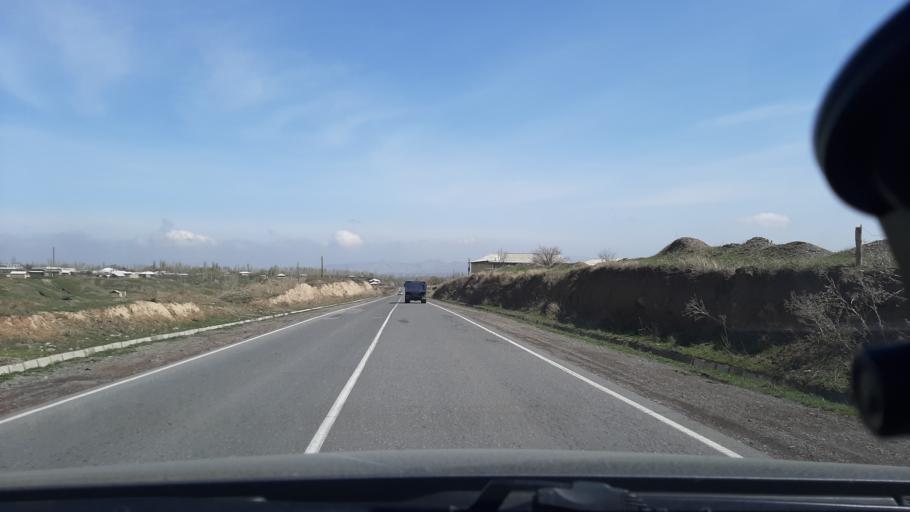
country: TJ
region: Viloyati Sughd
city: Shahriston
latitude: 39.7696
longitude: 68.8229
